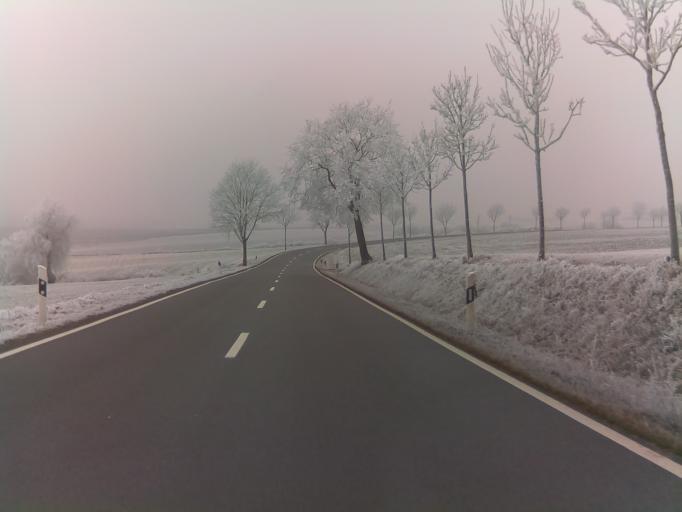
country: DE
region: Thuringia
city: Henneberg
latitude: 50.5166
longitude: 10.3107
